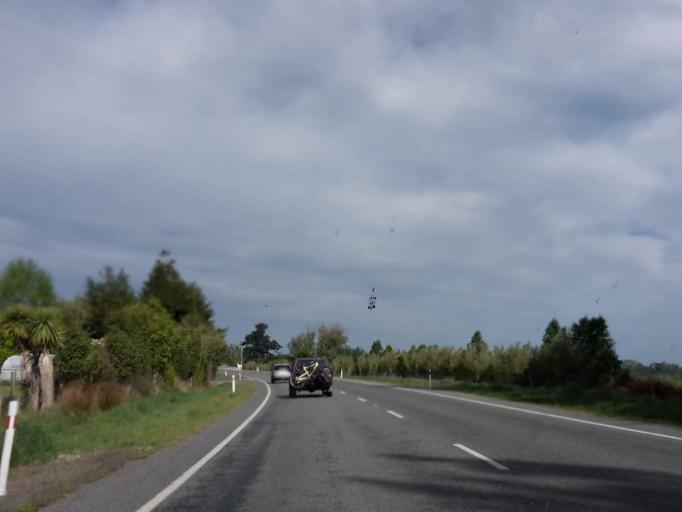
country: NZ
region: Canterbury
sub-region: Timaru District
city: Pleasant Point
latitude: -44.1168
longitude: 171.1760
